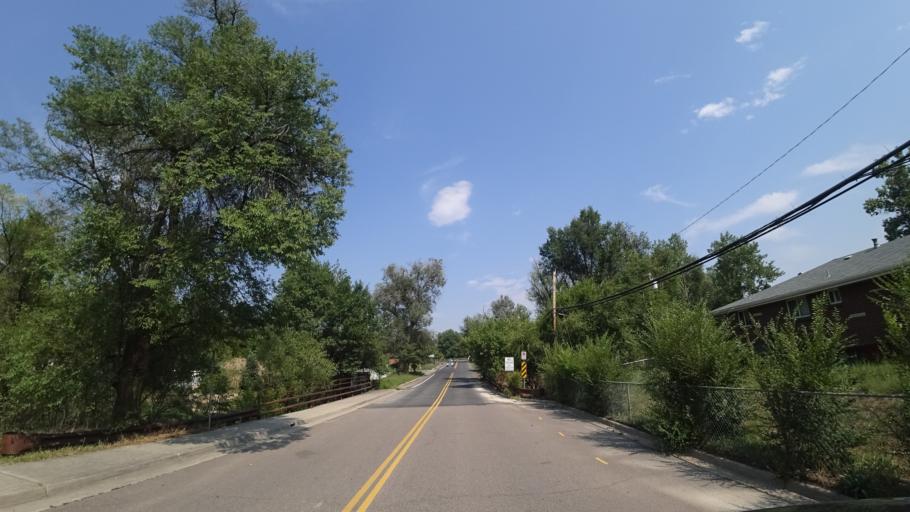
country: US
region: Colorado
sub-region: Arapahoe County
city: Greenwood Village
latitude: 39.6132
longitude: -104.9808
